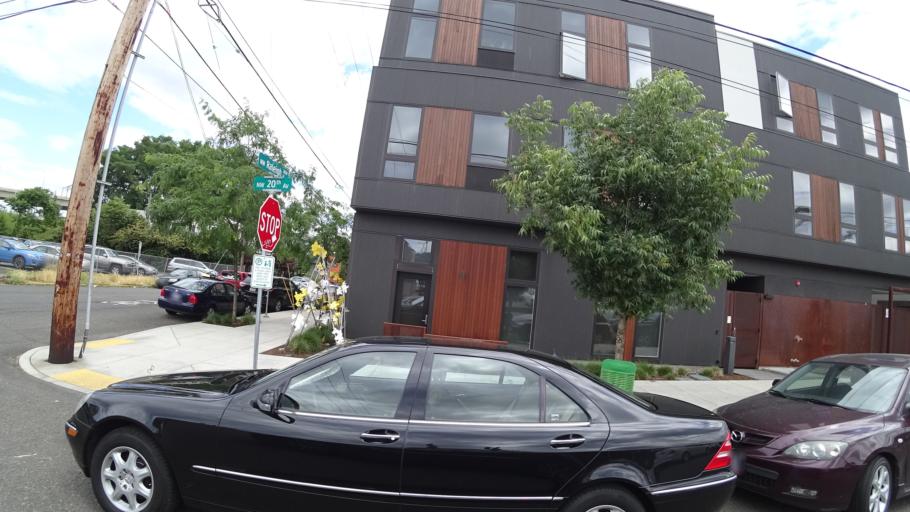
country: US
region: Oregon
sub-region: Multnomah County
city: Portland
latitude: 45.5340
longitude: -122.6927
